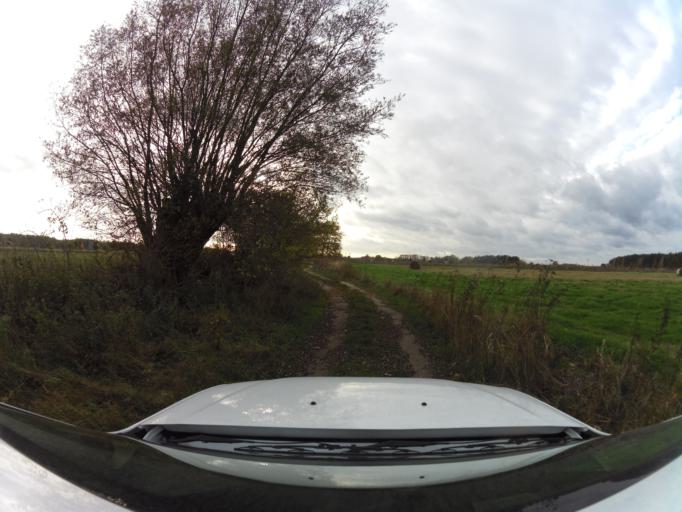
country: PL
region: West Pomeranian Voivodeship
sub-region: Powiat goleniowski
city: Nowogard
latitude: 53.6940
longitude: 15.0982
